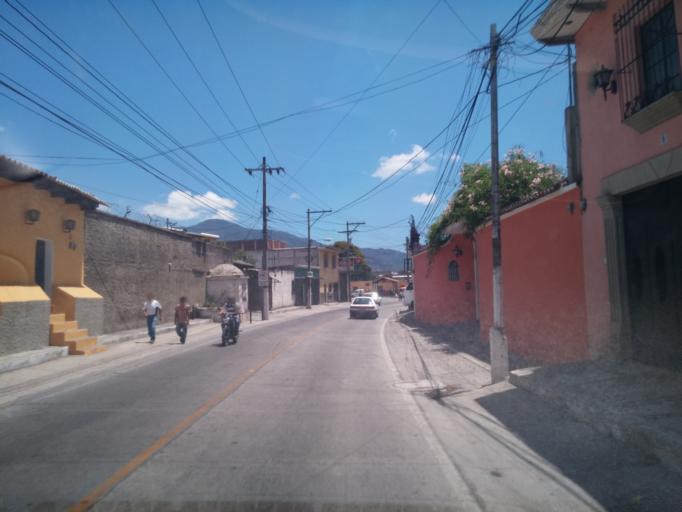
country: GT
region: Sacatepequez
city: Jocotenango
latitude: 14.5795
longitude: -90.7432
